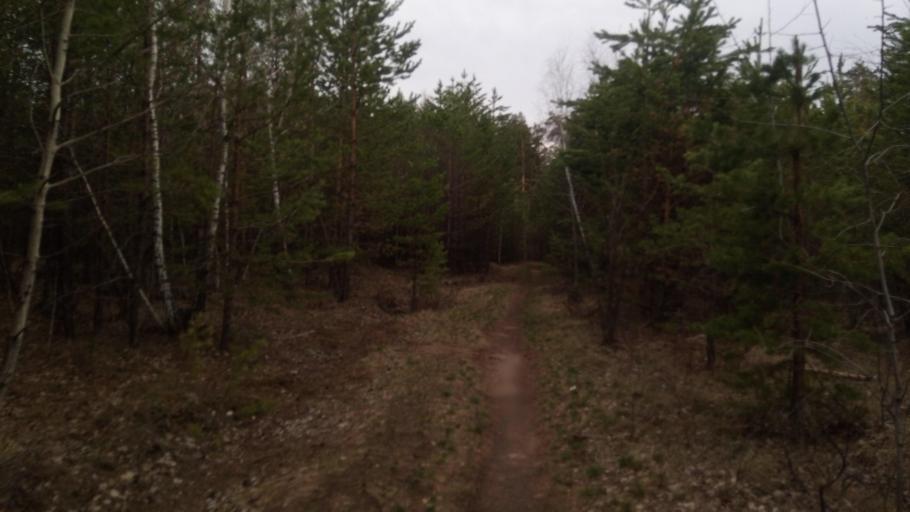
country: RU
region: Chelyabinsk
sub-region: Gorod Chelyabinsk
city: Chelyabinsk
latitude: 55.1386
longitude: 61.3400
